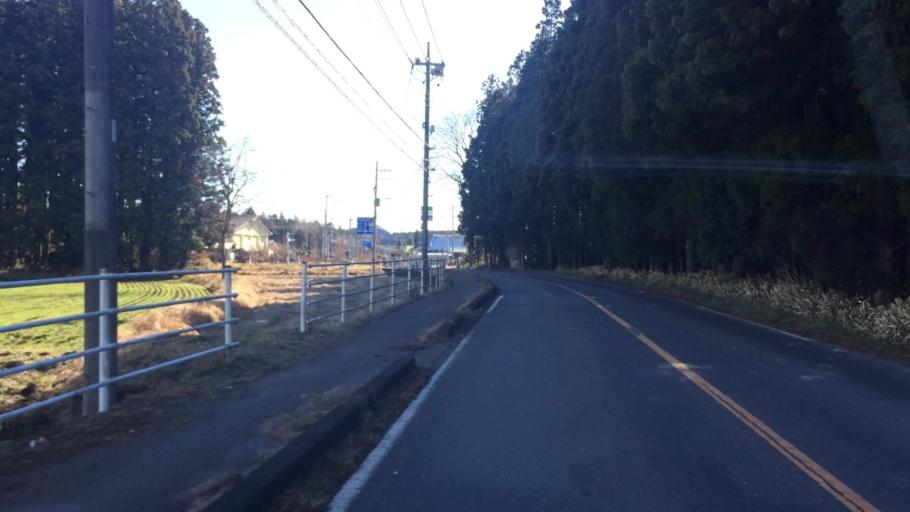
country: JP
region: Tochigi
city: Imaichi
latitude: 36.7507
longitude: 139.7341
